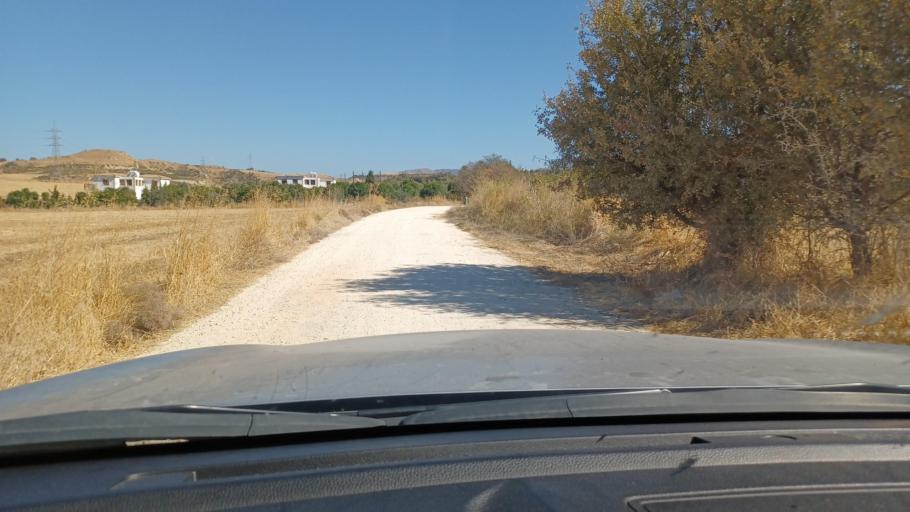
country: CY
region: Pafos
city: Polis
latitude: 35.0228
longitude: 32.4488
